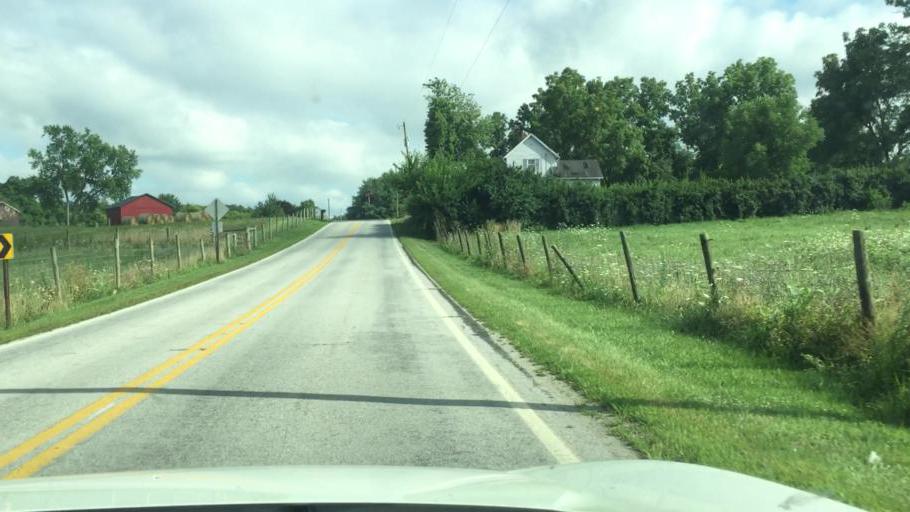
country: US
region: Ohio
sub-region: Clark County
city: Northridge
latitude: 39.9894
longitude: -83.6867
